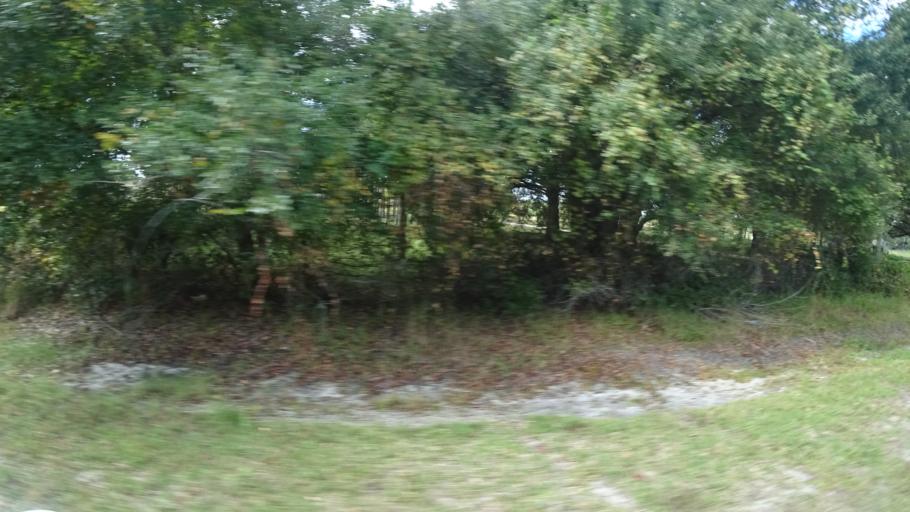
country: US
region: Florida
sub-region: Sarasota County
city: Warm Mineral Springs
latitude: 27.2699
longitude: -82.1173
